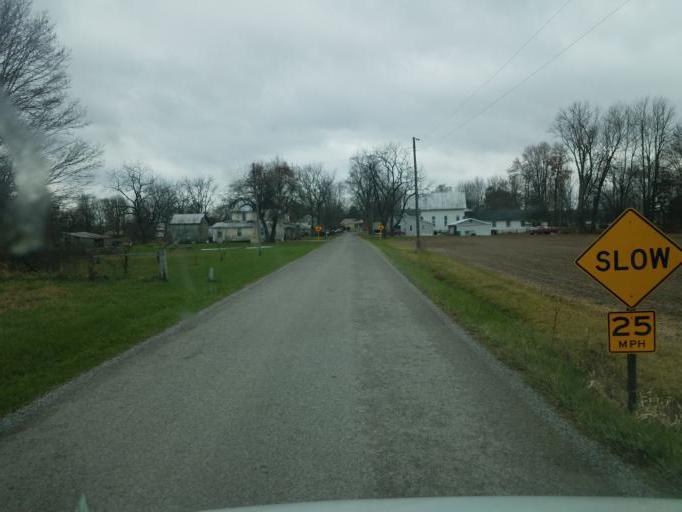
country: US
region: Ohio
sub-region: Licking County
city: Johnstown
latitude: 40.2108
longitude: -82.6149
